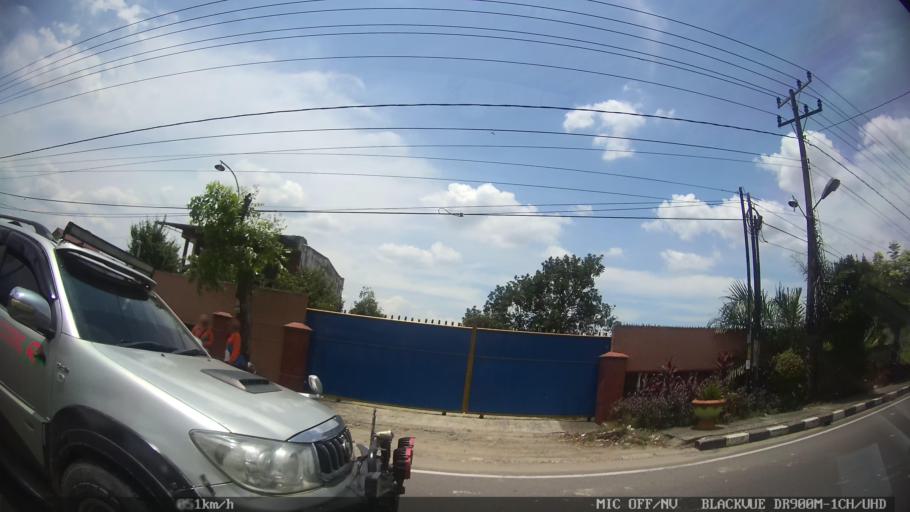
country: ID
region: North Sumatra
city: Binjai
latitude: 3.6061
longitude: 98.5289
